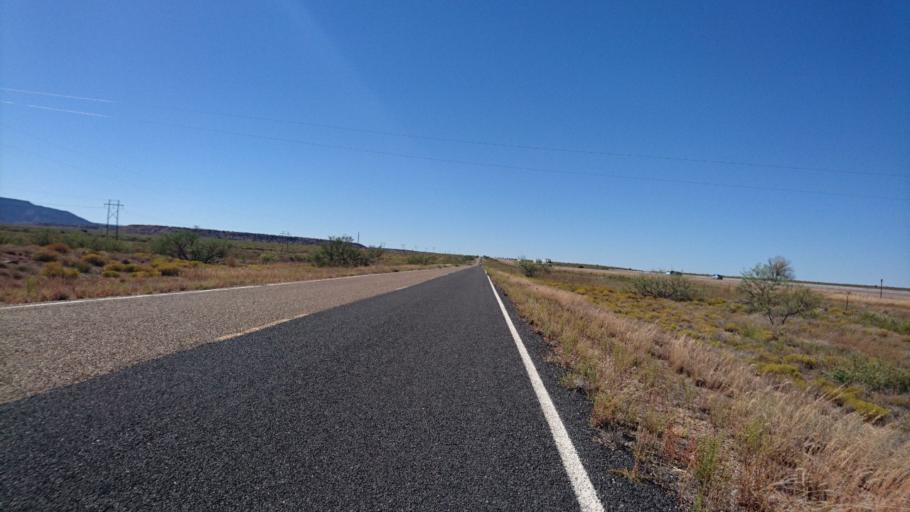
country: US
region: New Mexico
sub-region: Quay County
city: Tucumcari
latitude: 35.0839
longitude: -104.1073
